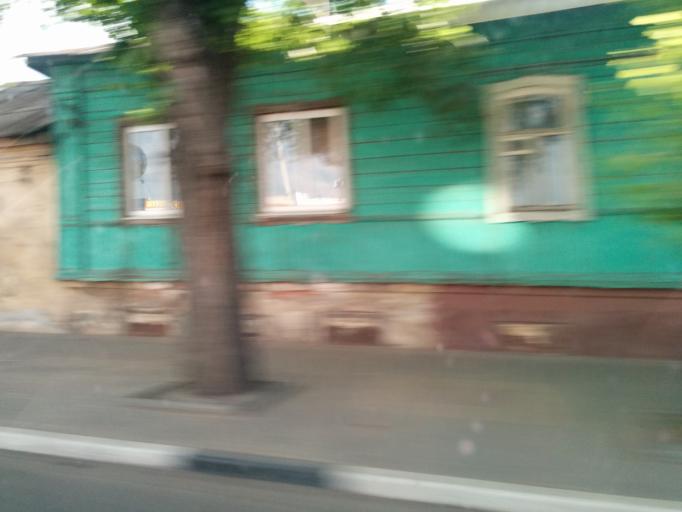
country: RU
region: Tambov
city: Tambov
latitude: 52.7231
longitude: 41.4369
